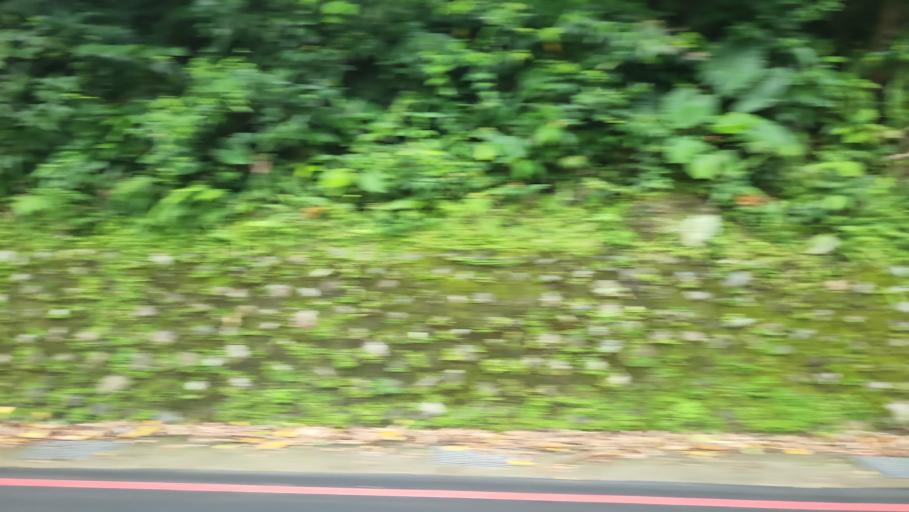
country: TW
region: Taiwan
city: Daxi
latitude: 24.8654
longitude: 121.4217
